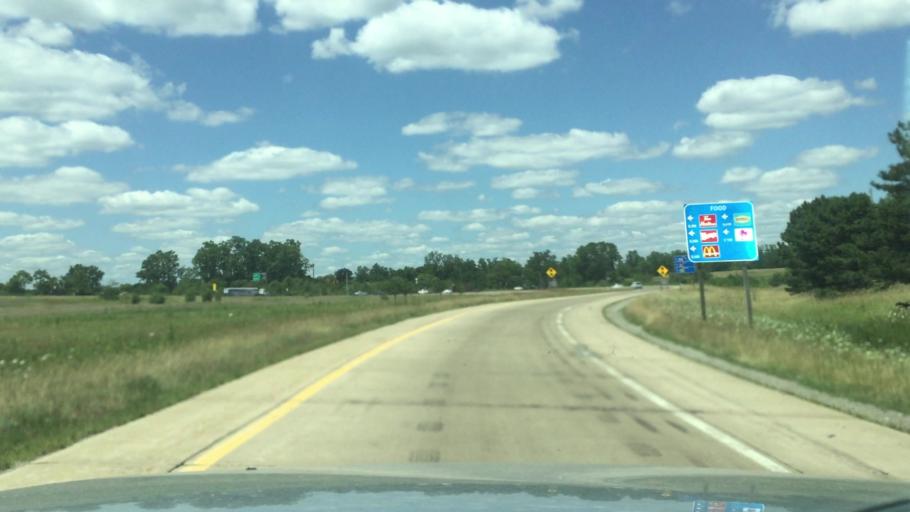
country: US
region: Michigan
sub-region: Wayne County
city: Belleville
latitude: 42.2192
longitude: -83.5425
